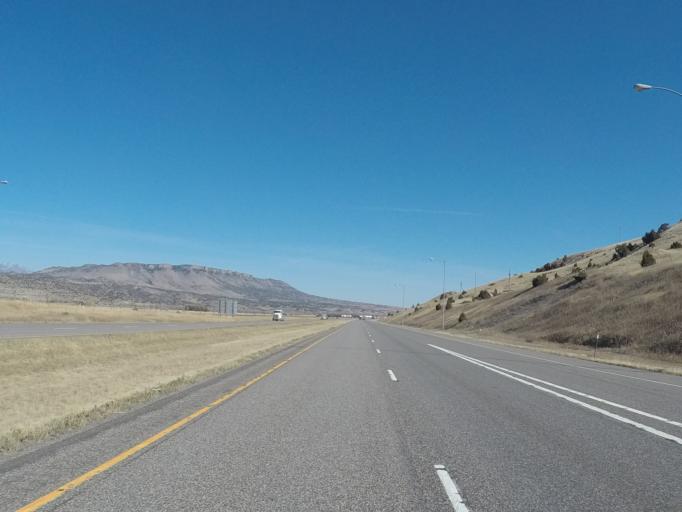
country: US
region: Montana
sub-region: Park County
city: Livingston
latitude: 45.7081
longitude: -110.4514
